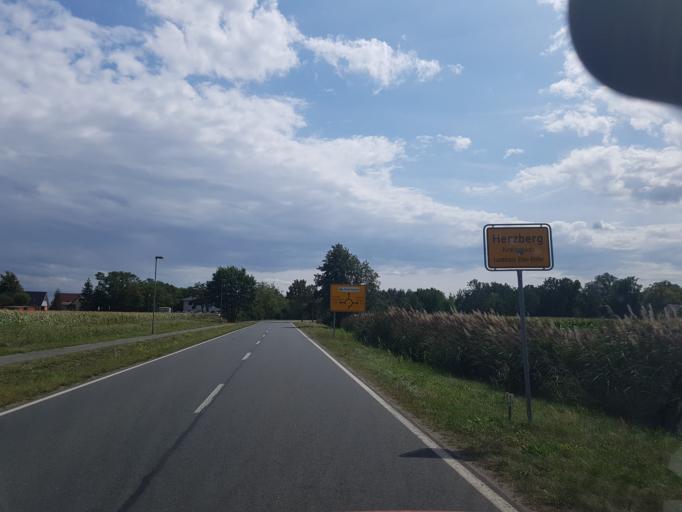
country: DE
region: Brandenburg
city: Herzberg
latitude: 51.6826
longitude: 13.2051
